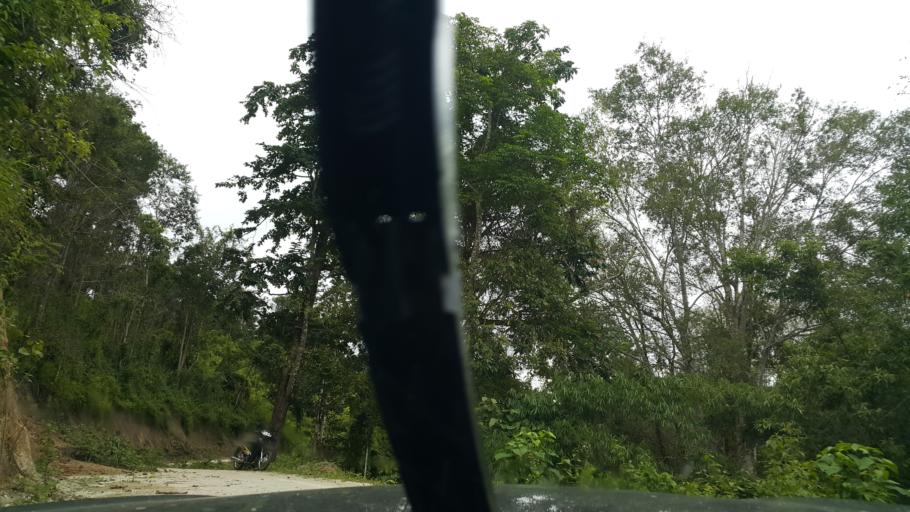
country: TH
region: Chiang Mai
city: Samoeng
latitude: 18.8020
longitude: 98.6251
